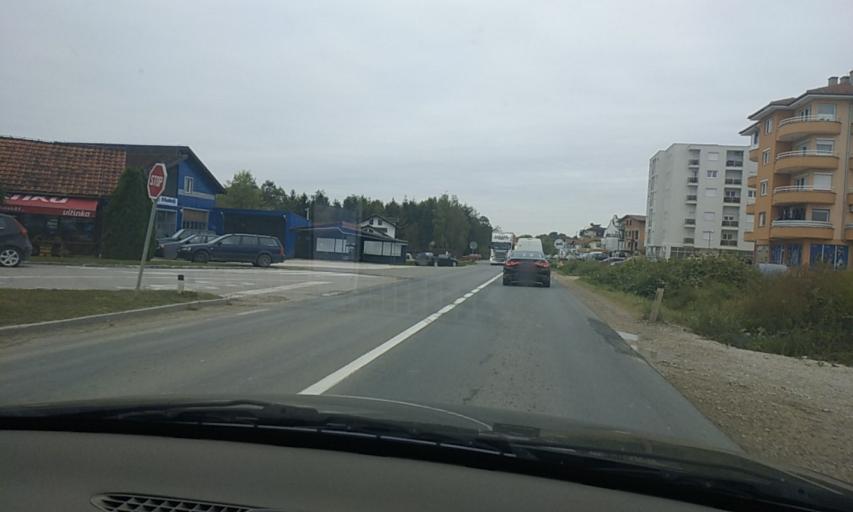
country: BA
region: Republika Srpska
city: Prnjavor
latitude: 44.8626
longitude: 17.6694
